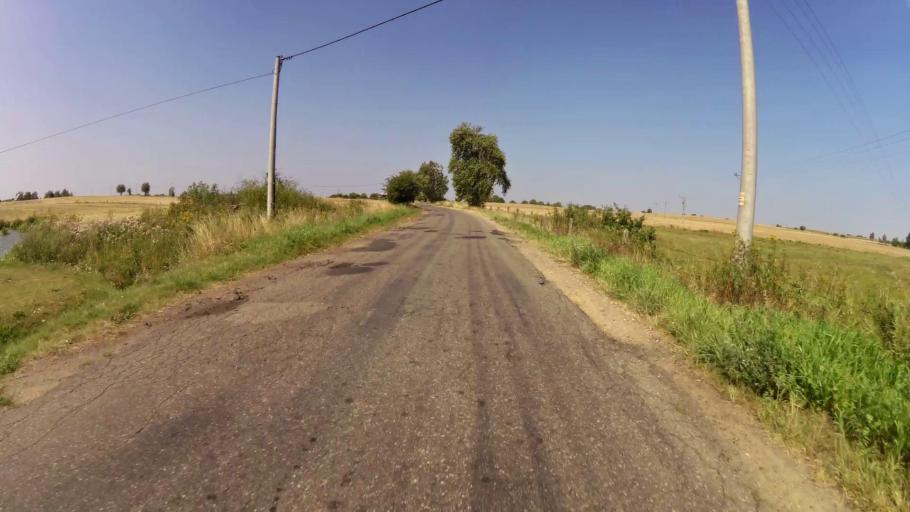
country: PL
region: West Pomeranian Voivodeship
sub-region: Powiat walecki
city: Walcz
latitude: 53.2208
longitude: 16.4707
